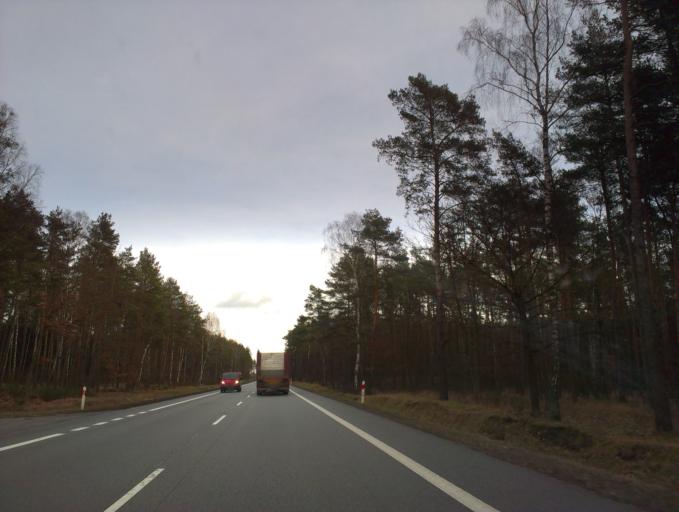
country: PL
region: Kujawsko-Pomorskie
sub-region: Powiat lipnowski
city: Skepe
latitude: 52.8845
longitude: 19.3911
